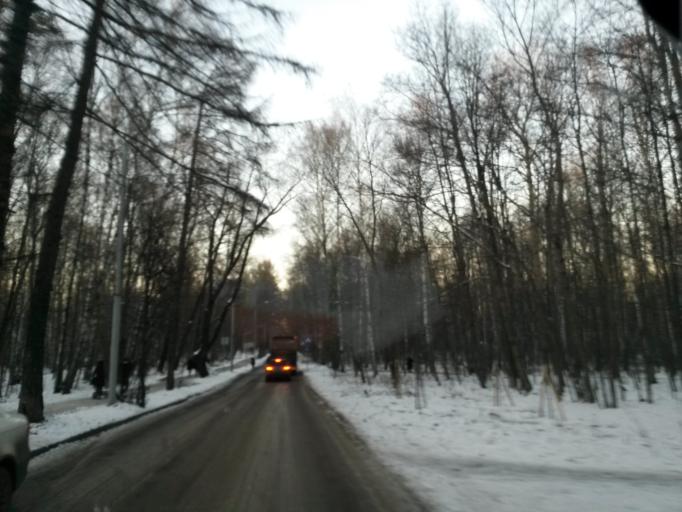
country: RU
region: Moscow
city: Sokol'niki
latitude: 55.8031
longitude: 37.6708
